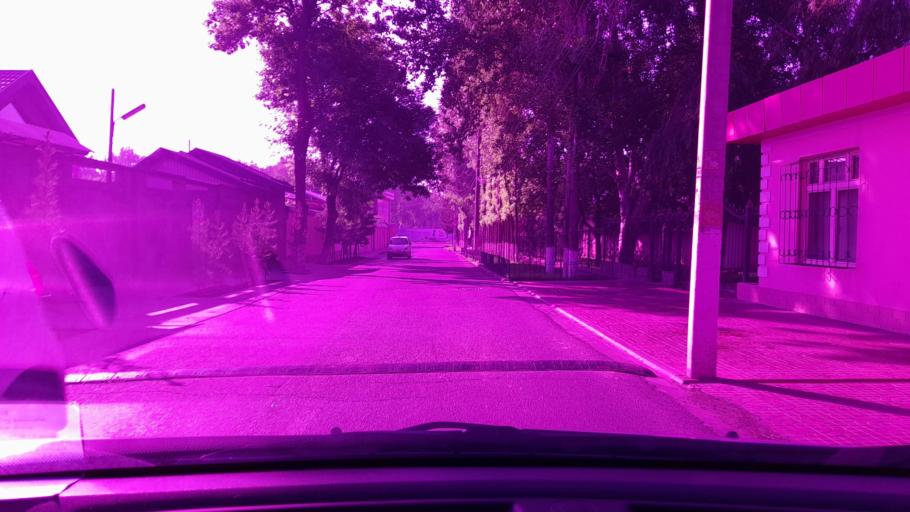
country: UZ
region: Toshkent
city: Salor
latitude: 41.3337
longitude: 69.3617
